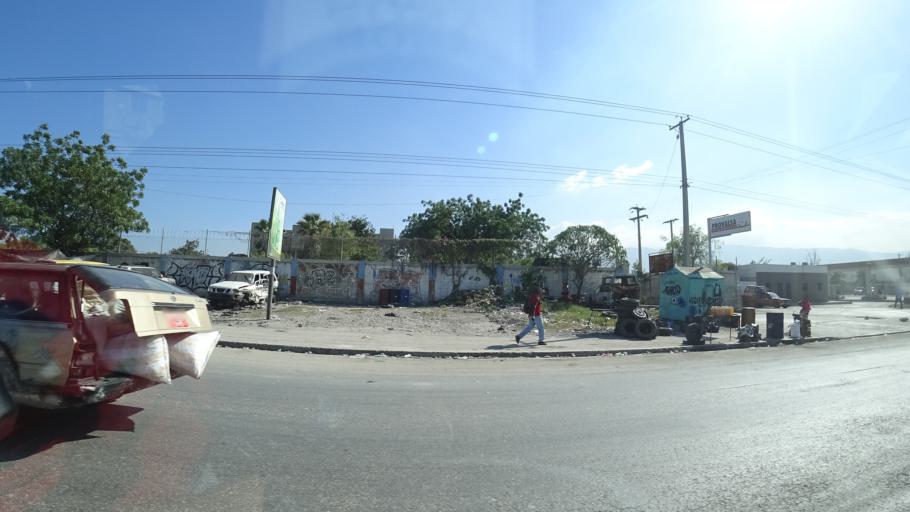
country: HT
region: Ouest
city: Delmas 73
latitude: 18.5792
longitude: -72.3142
